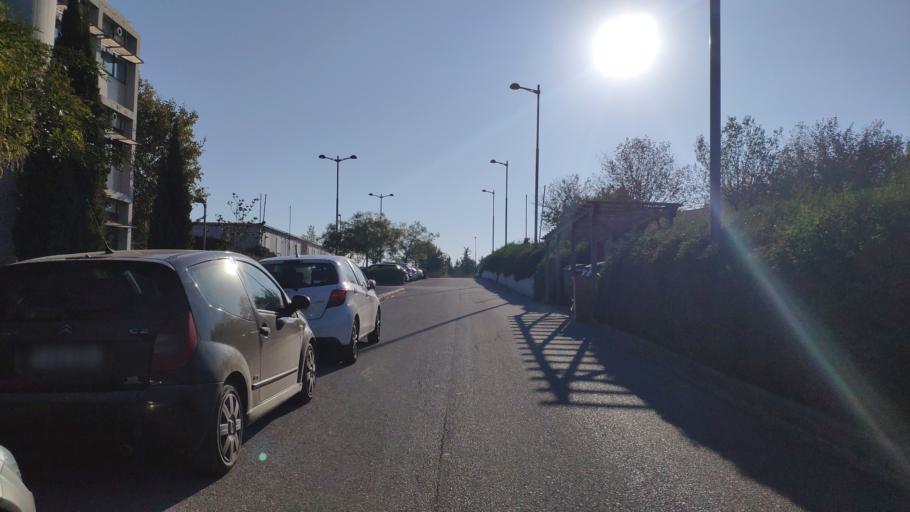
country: GR
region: Thessaly
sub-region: Nomos Larisis
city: Terpsithea
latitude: 39.6139
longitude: 22.3878
